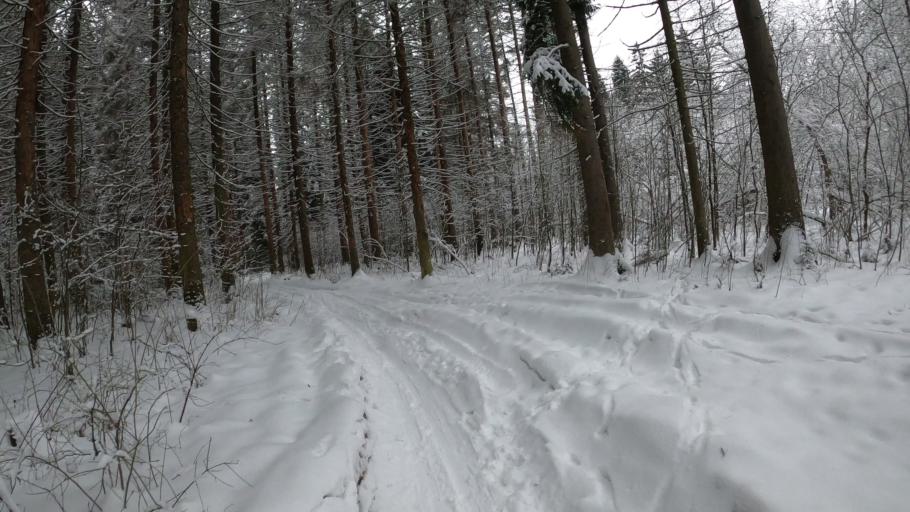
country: RU
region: Moskovskaya
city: Firsanovka
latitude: 55.9524
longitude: 37.2219
